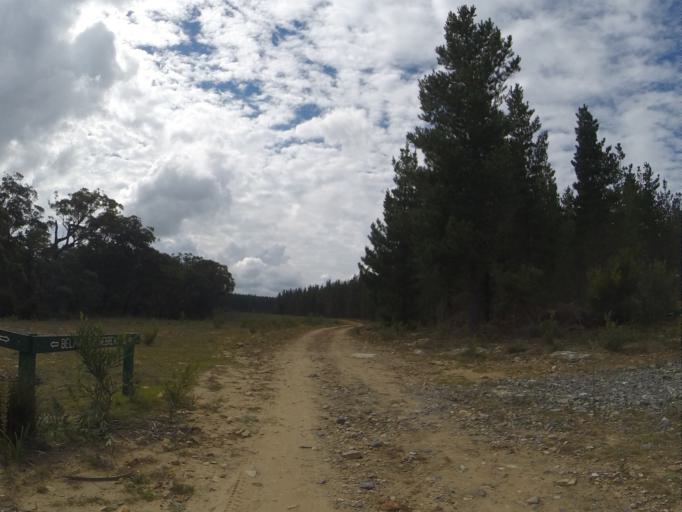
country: AU
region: New South Wales
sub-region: Wingecarribee
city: Moss Vale
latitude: -34.5201
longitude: 150.2257
